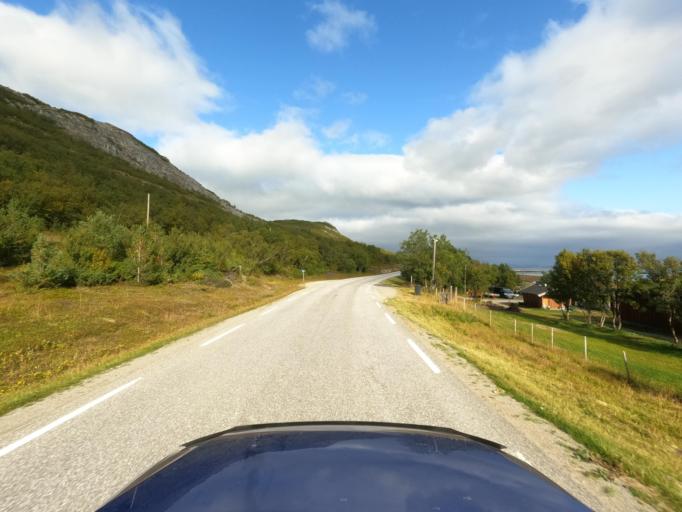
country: NO
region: Finnmark Fylke
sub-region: Porsanger
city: Lakselv
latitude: 70.2456
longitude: 24.9945
